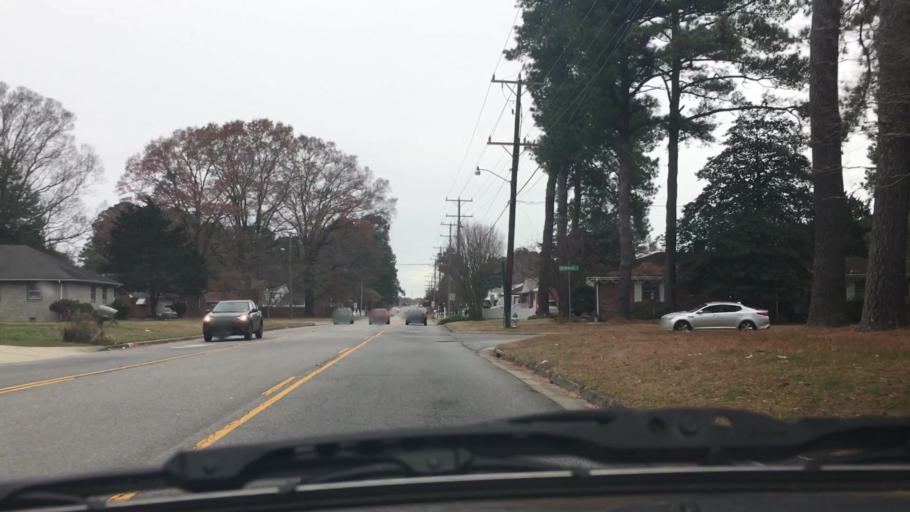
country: US
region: Virginia
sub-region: City of Portsmouth
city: Portsmouth Heights
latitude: 36.8643
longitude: -76.3771
